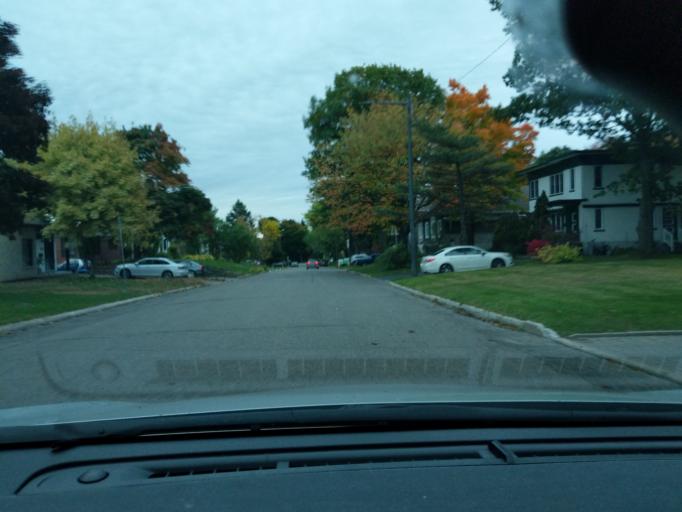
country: CA
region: Quebec
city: Quebec
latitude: 46.7667
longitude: -71.2781
